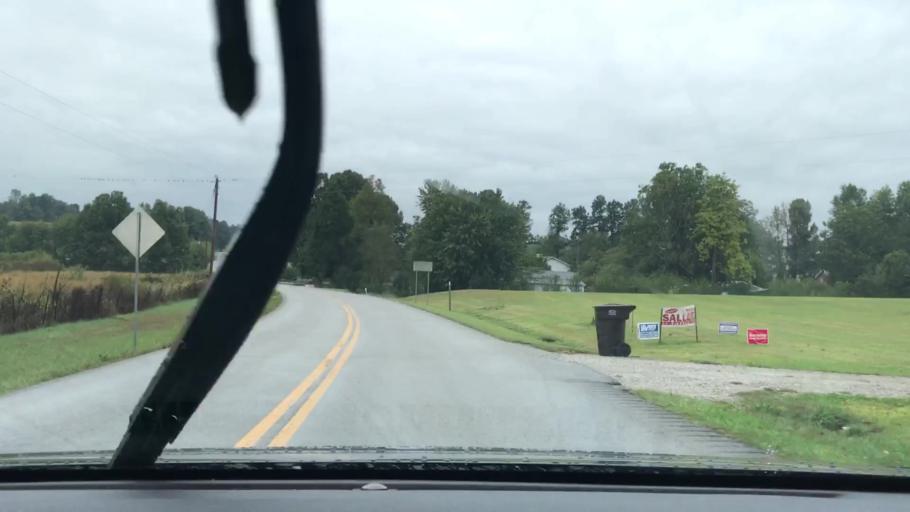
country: US
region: Kentucky
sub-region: McLean County
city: Calhoun
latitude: 37.4852
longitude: -87.2478
